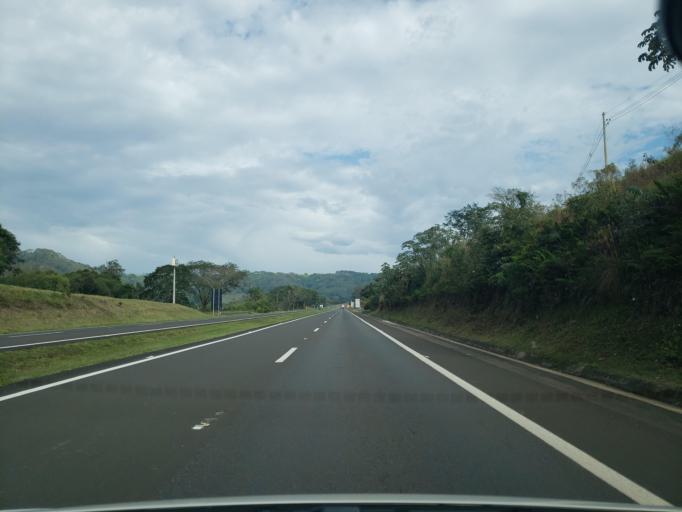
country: BR
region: Sao Paulo
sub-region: Dois Corregos
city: Dois Corregos
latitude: -22.2461
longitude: -48.3291
